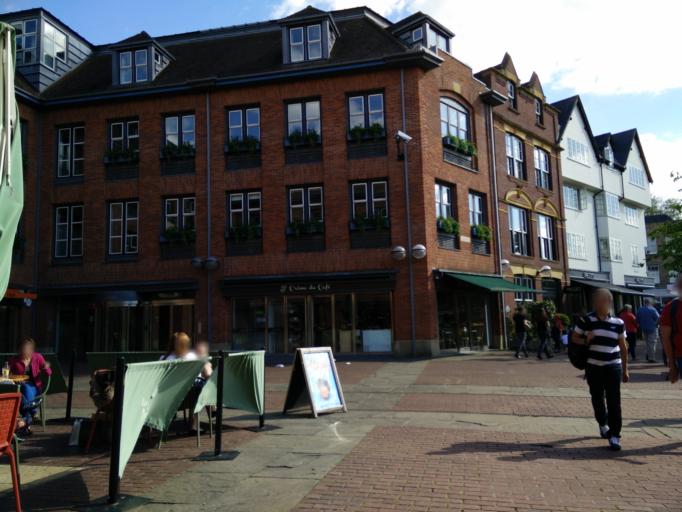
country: GB
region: England
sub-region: Cambridgeshire
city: Cambridge
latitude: 52.2102
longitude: 0.1173
